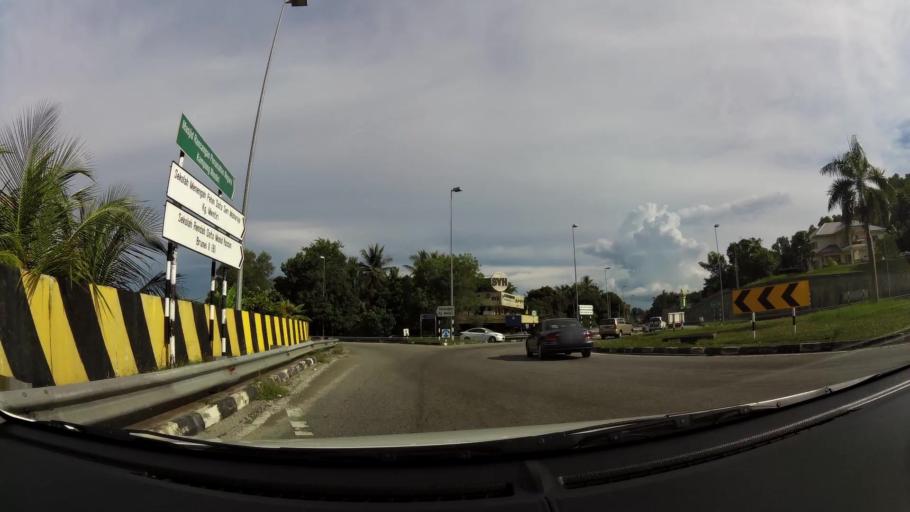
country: BN
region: Brunei and Muara
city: Bandar Seri Begawan
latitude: 4.9707
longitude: 115.0209
